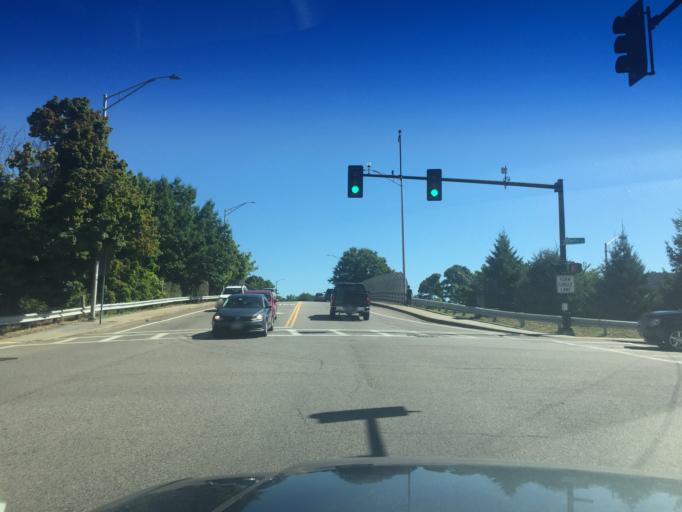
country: US
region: Massachusetts
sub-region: Norfolk County
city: Quincy
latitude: 42.2406
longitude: -71.0062
